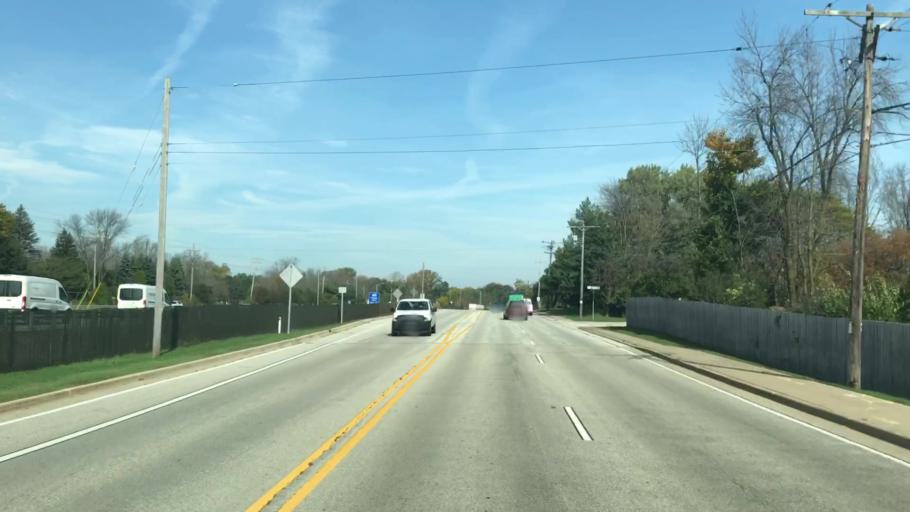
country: US
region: Wisconsin
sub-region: Milwaukee County
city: River Hills
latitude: 43.1876
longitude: -87.9224
